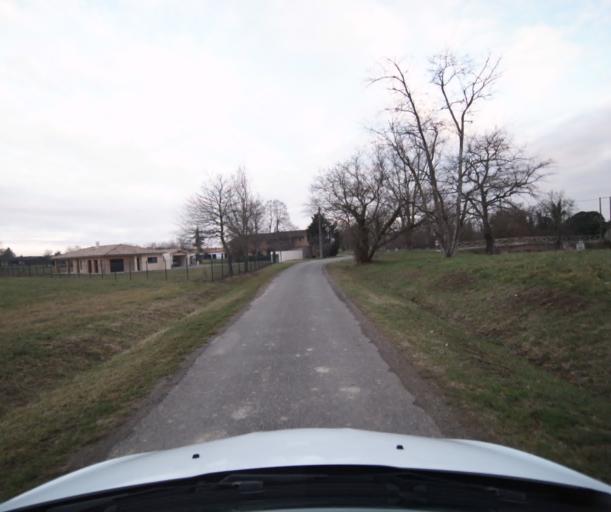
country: FR
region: Midi-Pyrenees
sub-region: Departement du Tarn-et-Garonne
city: Castelsarrasin
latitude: 44.0665
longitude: 1.1010
